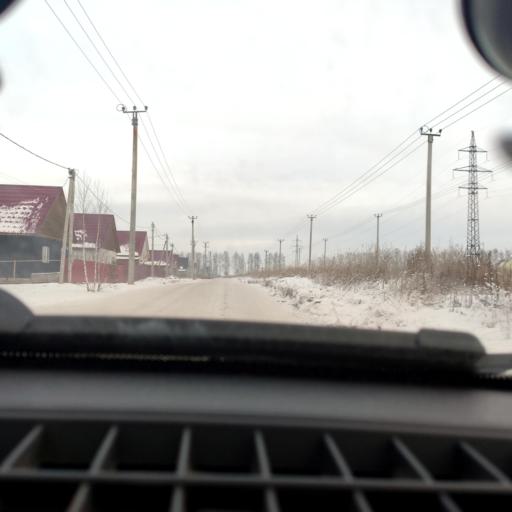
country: RU
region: Bashkortostan
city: Iglino
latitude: 54.8271
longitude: 56.4387
